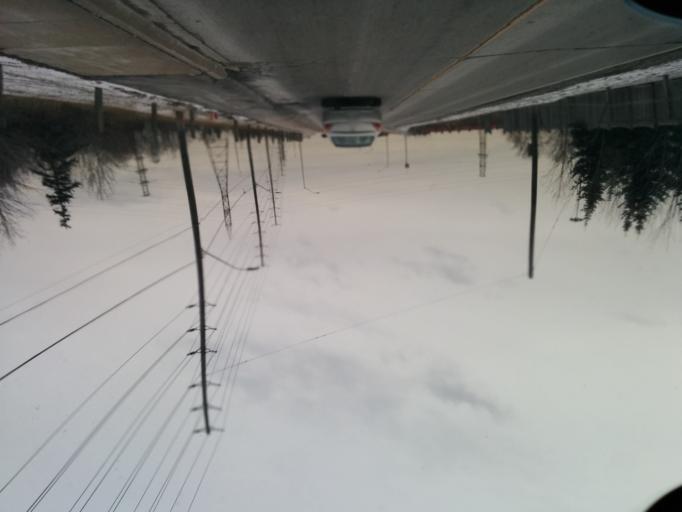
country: CA
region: Ontario
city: Mississauga
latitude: 43.5601
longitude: -79.6843
